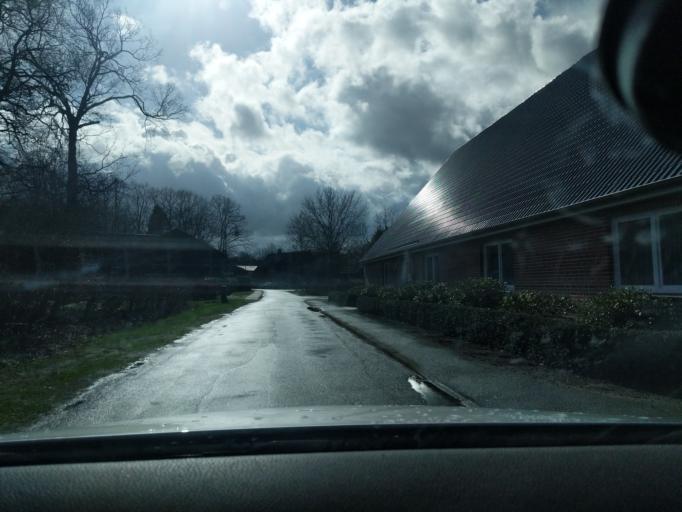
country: DE
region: Lower Saxony
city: Kranenburg
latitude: 53.6075
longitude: 9.2070
